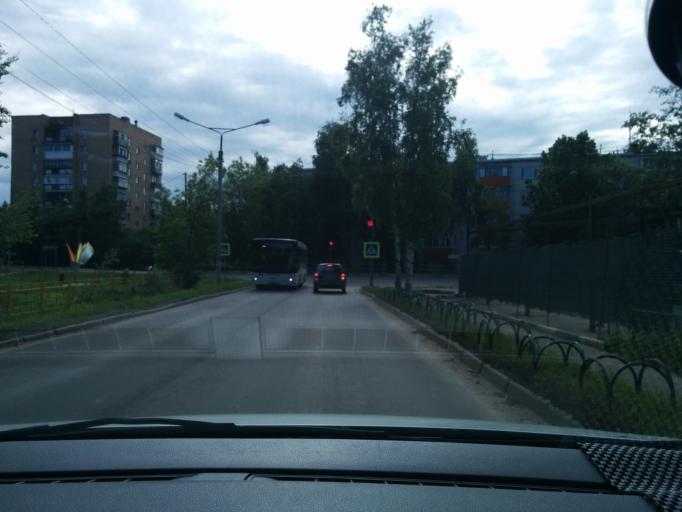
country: RU
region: Moskovskaya
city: Lobnya
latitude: 56.0158
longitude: 37.4700
